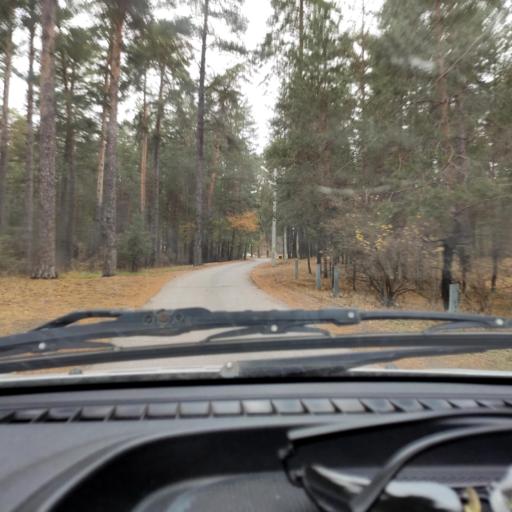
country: RU
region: Samara
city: Tol'yatti
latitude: 53.4747
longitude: 49.3338
